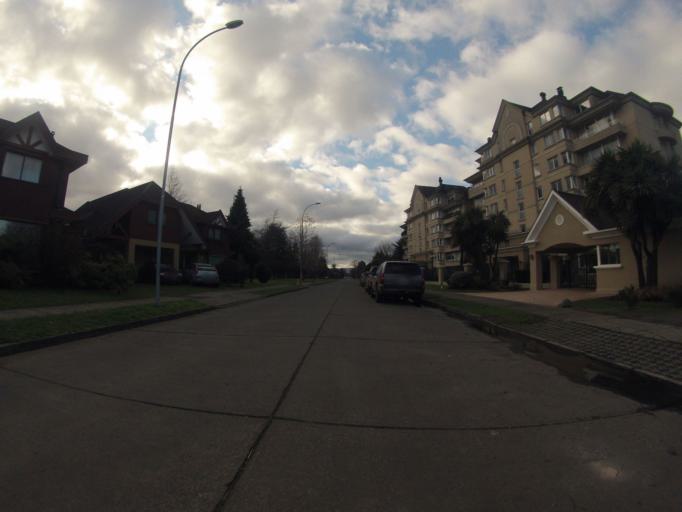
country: CL
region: Araucania
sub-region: Provincia de Cautin
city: Temuco
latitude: -38.7405
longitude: -72.6392
